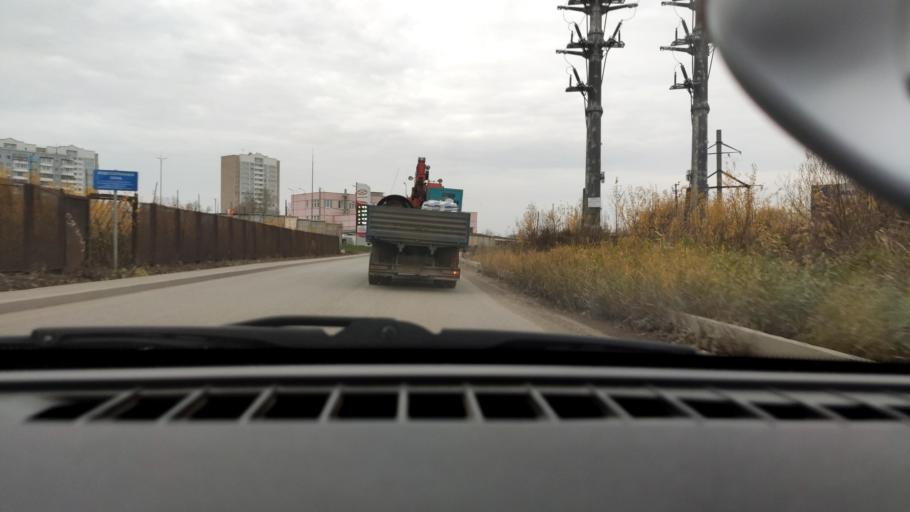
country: RU
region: Perm
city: Kondratovo
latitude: 58.0024
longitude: 56.1384
